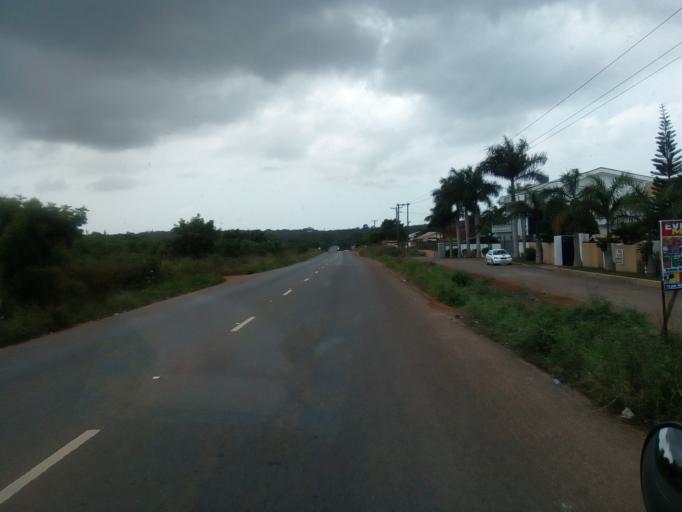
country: GH
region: Greater Accra
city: Dome
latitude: 5.6502
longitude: -0.2052
